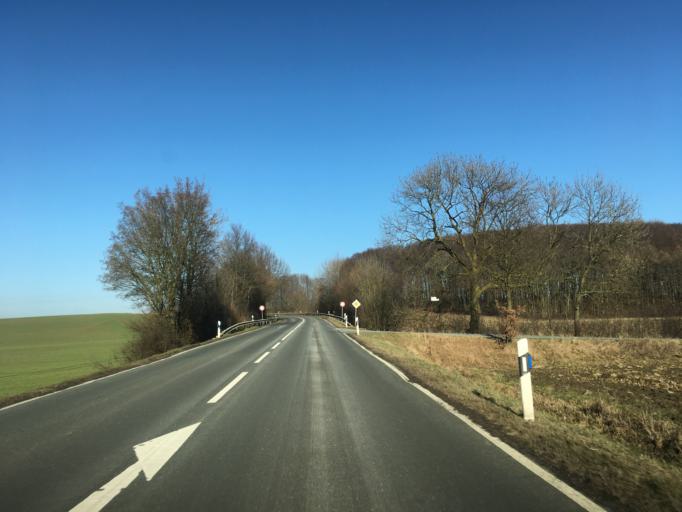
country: DE
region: North Rhine-Westphalia
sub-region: Regierungsbezirk Munster
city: Horstmar
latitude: 52.0712
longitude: 7.2926
